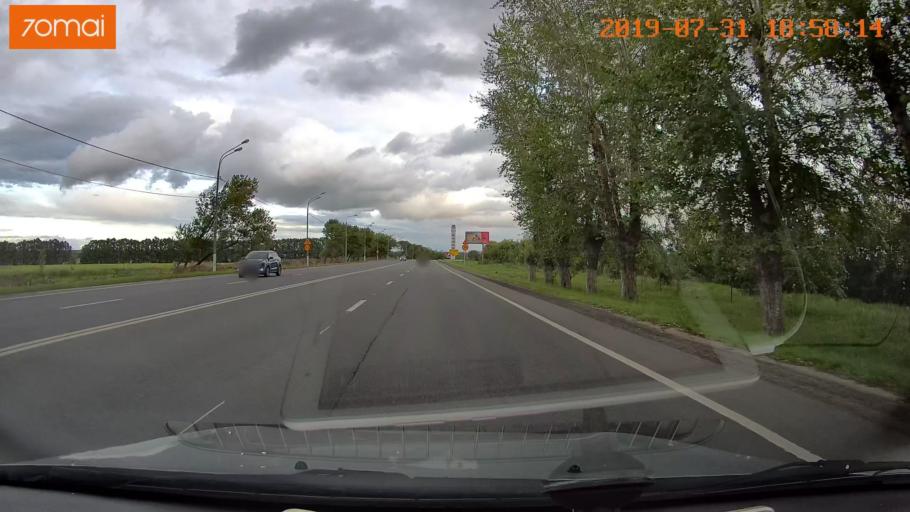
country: RU
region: Moskovskaya
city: Raduzhnyy
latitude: 55.1484
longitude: 38.7020
